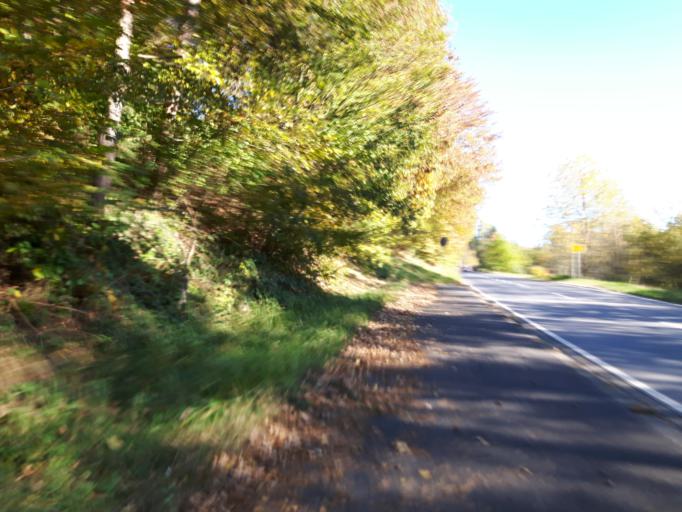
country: DE
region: Bavaria
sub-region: Regierungsbezirk Unterfranken
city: Heimbuchenthal
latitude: 49.8949
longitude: 9.2623
